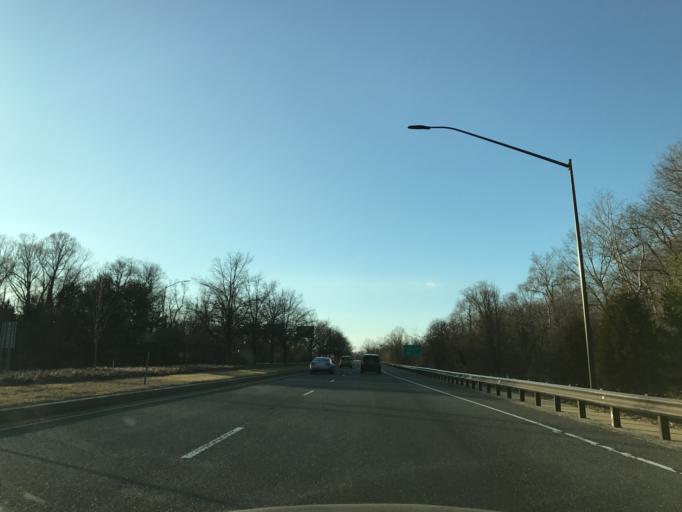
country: US
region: Maryland
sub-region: Anne Arundel County
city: Parole
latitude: 38.9958
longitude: -76.5173
